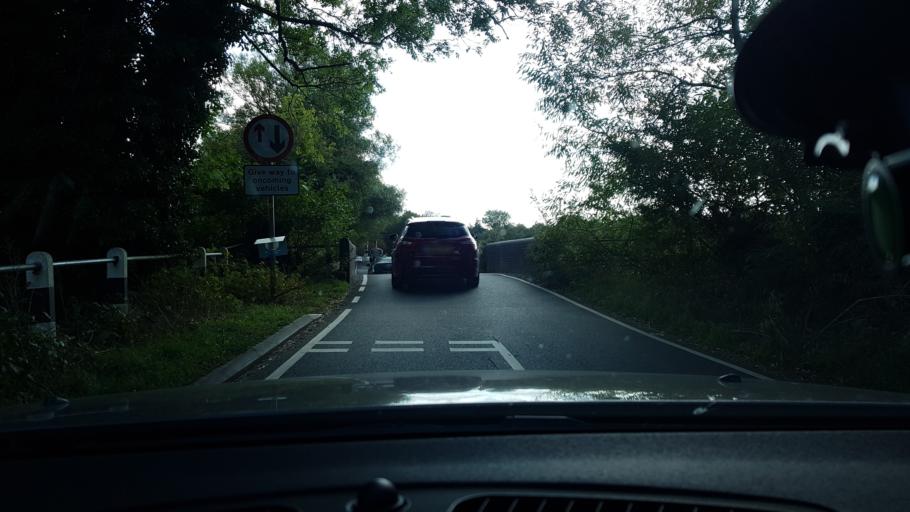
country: GB
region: England
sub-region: West Berkshire
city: Kintbury
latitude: 51.4045
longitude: -1.4460
